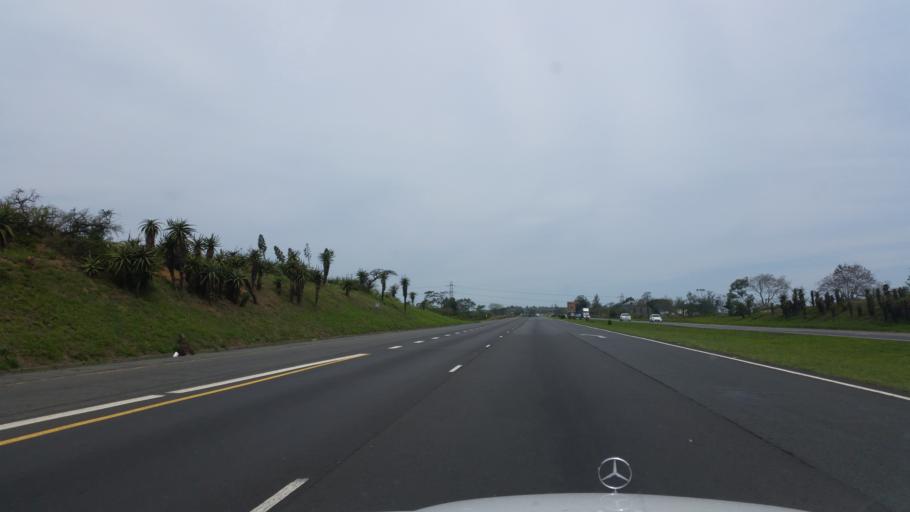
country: ZA
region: KwaZulu-Natal
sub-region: uMgungundlovu District Municipality
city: Camperdown
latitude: -29.6935
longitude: 30.4839
